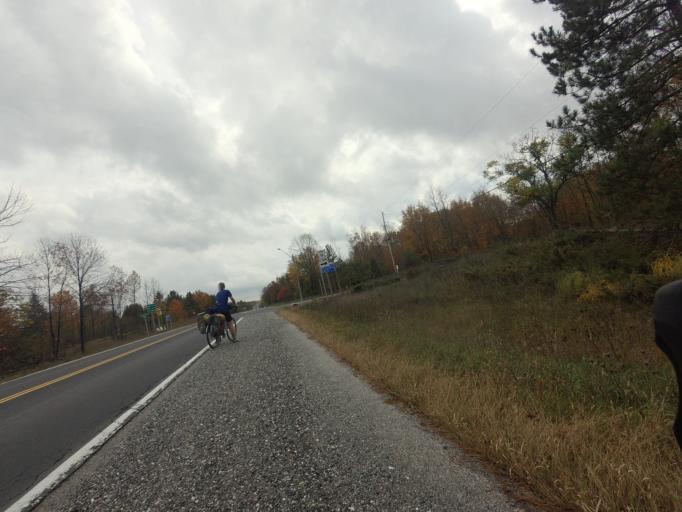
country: CA
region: Ontario
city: Perth
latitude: 45.0945
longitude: -76.4613
